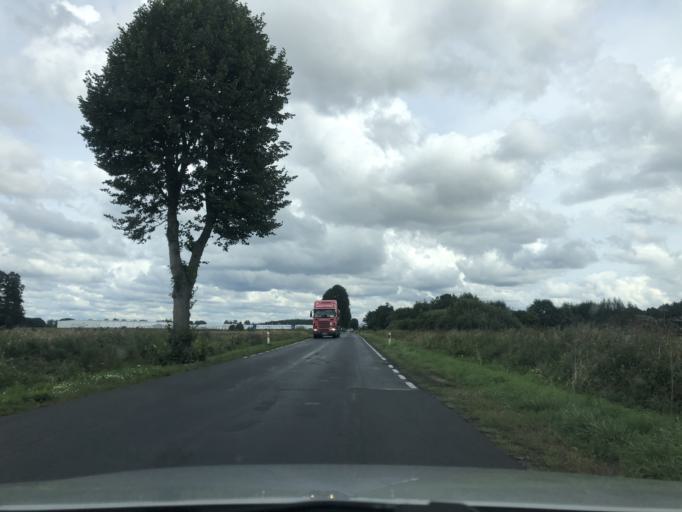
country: PL
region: Greater Poland Voivodeship
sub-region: Powiat czarnkowsko-trzcianecki
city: Krzyz Wielkopolski
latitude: 52.9043
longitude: 16.0468
